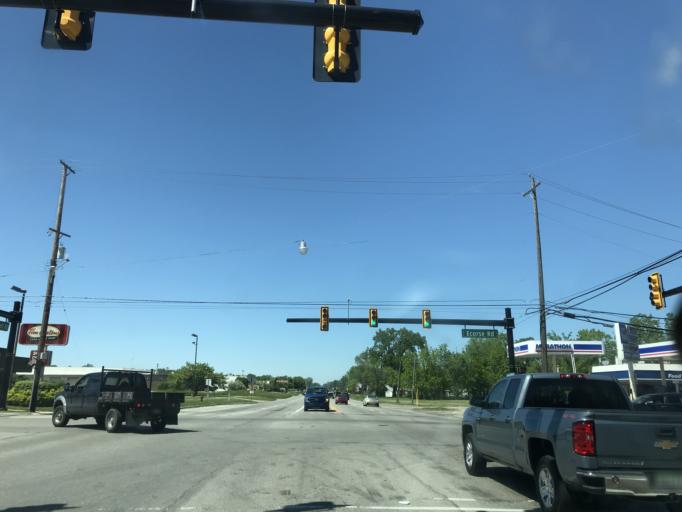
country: US
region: Michigan
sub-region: Wayne County
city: Inkster
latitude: 42.2531
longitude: -83.3284
